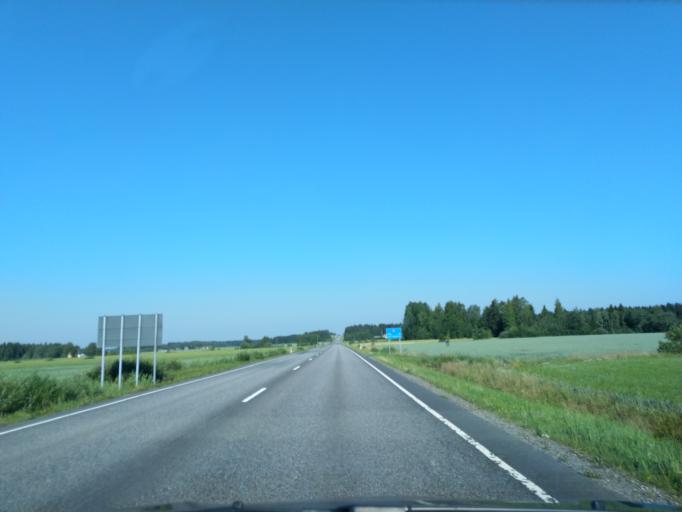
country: FI
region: Varsinais-Suomi
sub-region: Loimaa
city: Alastaro
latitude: 61.0424
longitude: 22.9891
